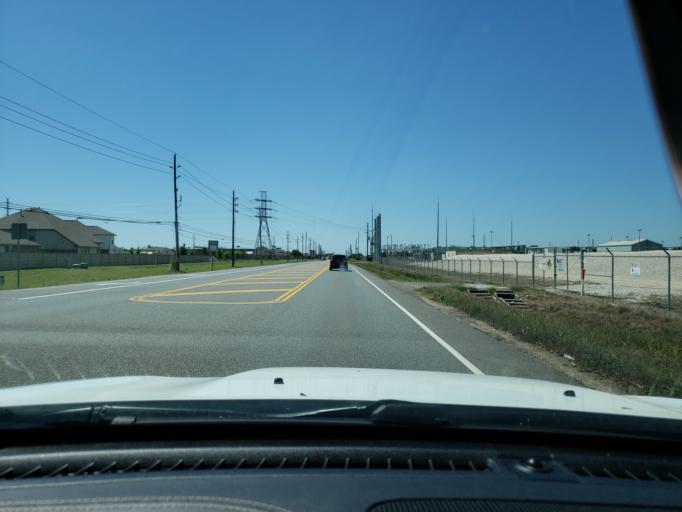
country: US
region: Texas
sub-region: Fort Bend County
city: Fulshear
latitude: 29.7040
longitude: -95.8461
